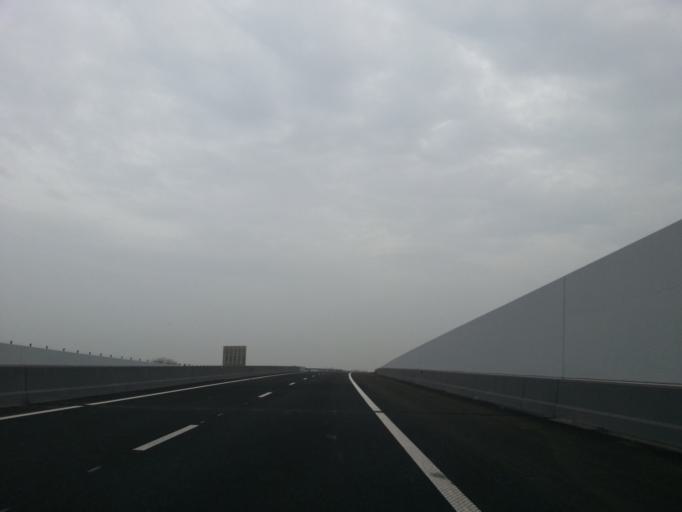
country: NL
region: North Brabant
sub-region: Gemeente Steenbergen
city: Steenbergen
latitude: 51.5982
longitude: 4.3105
